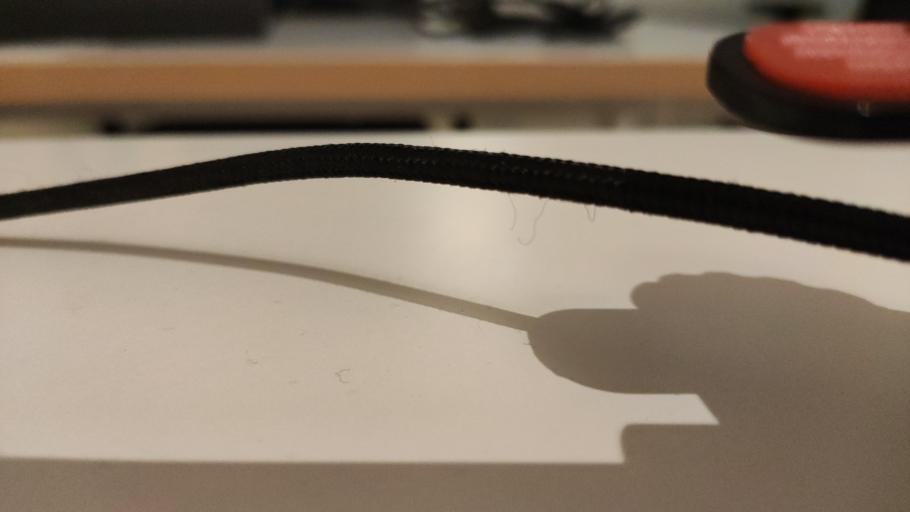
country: RU
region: Moskovskaya
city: Semkhoz
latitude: 56.3854
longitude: 38.0612
